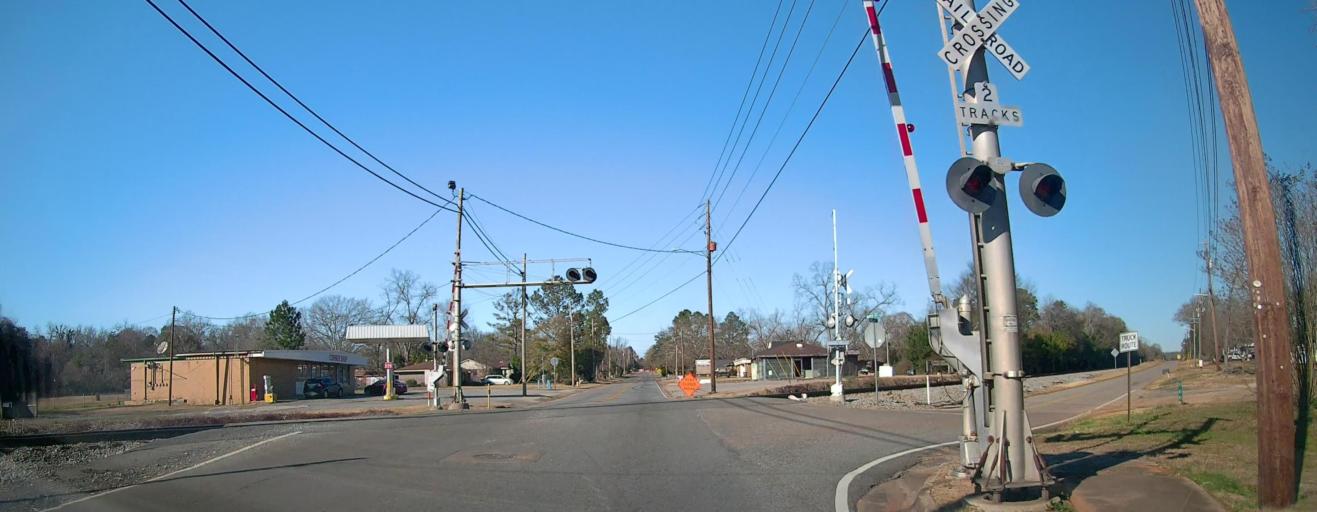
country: US
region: Georgia
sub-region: Sumter County
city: Americus
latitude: 32.0806
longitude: -84.2321
